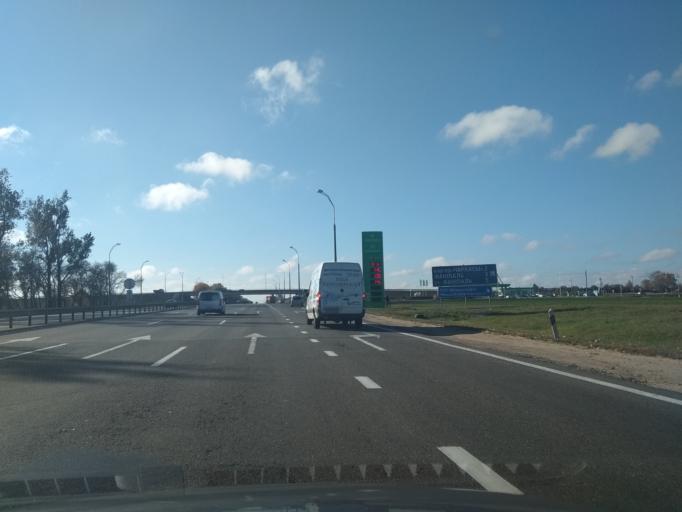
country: BY
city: Fanipol
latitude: 53.7711
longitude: 27.3500
